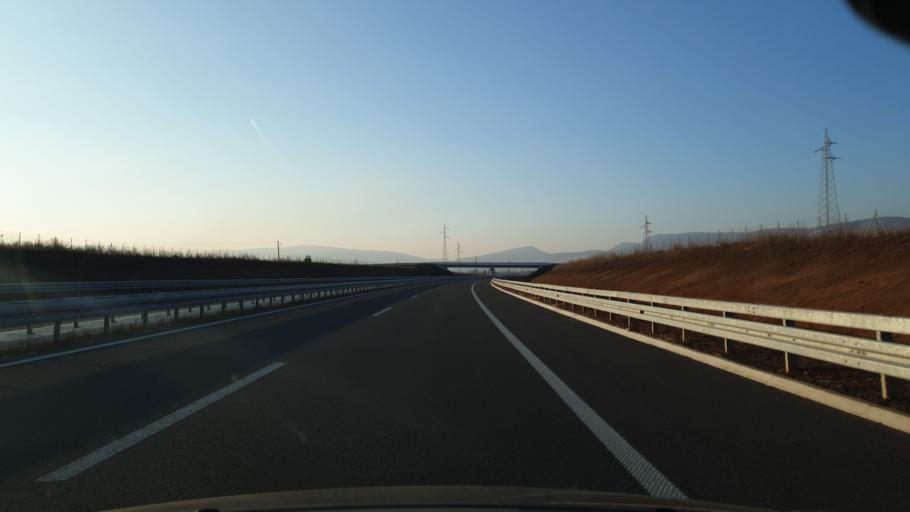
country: RS
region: Central Serbia
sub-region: Pirotski Okrug
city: Pirot
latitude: 43.1281
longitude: 22.5821
